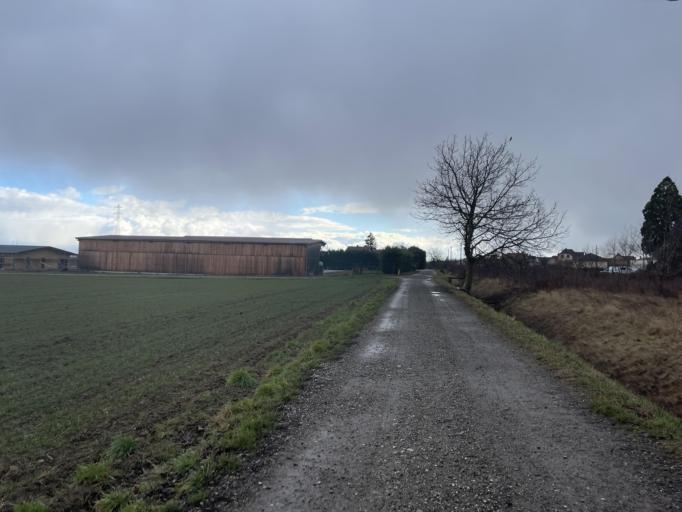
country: FR
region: Alsace
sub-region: Departement du Haut-Rhin
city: Soultz-Haut-Rhin
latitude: 47.8880
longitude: 7.2336
